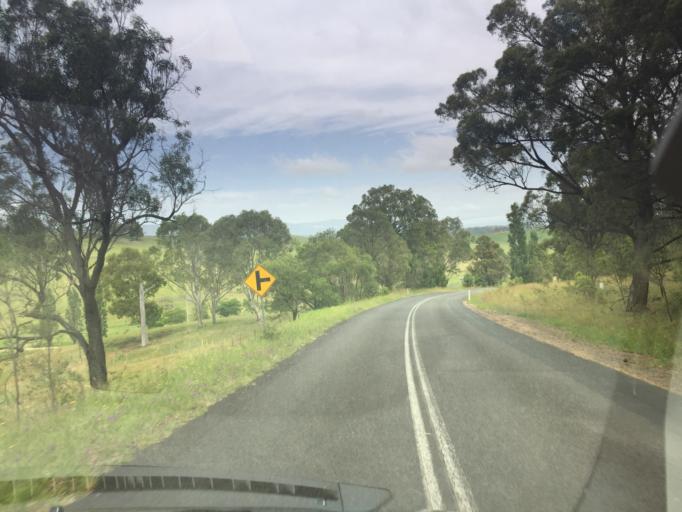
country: AU
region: New South Wales
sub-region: Bega Valley
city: Bega
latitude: -36.7538
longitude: 149.6699
